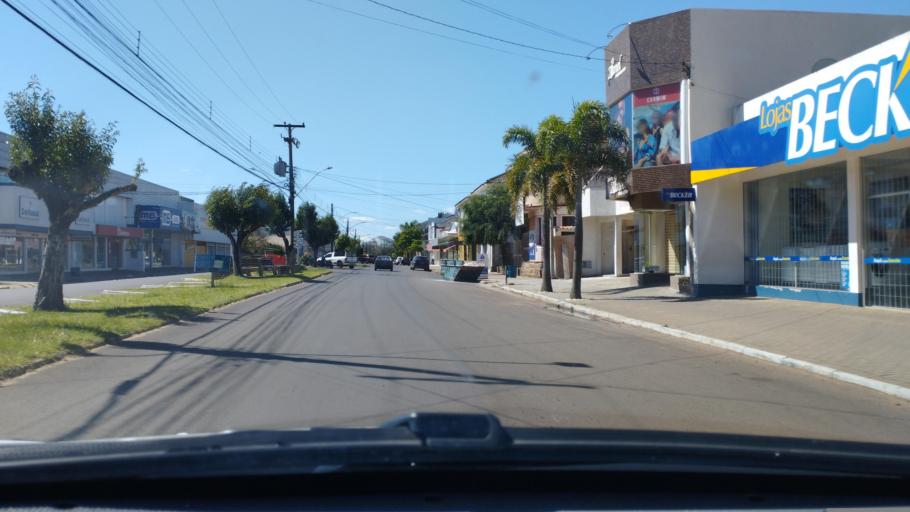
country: BR
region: Rio Grande do Sul
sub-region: Tupancireta
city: Tupancireta
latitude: -29.0799
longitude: -53.8372
